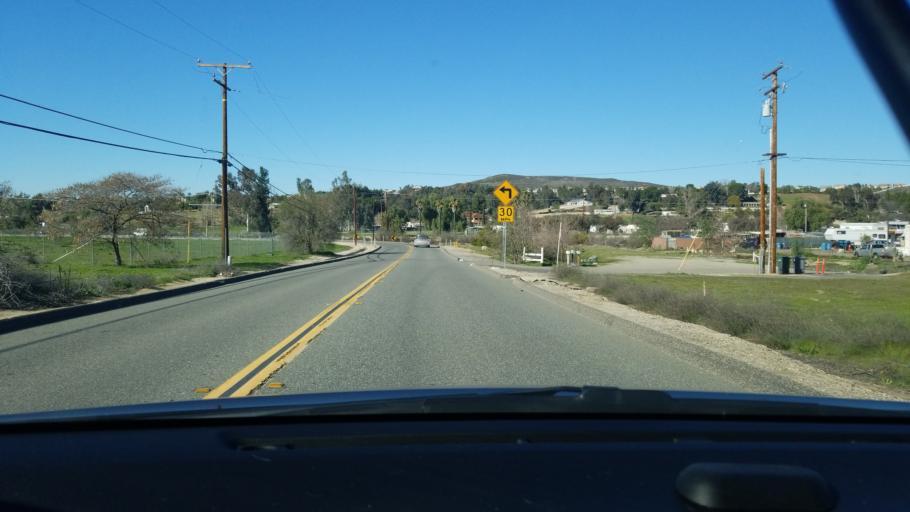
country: US
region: California
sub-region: Riverside County
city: Murrieta Hot Springs
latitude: 33.5421
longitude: -117.1112
